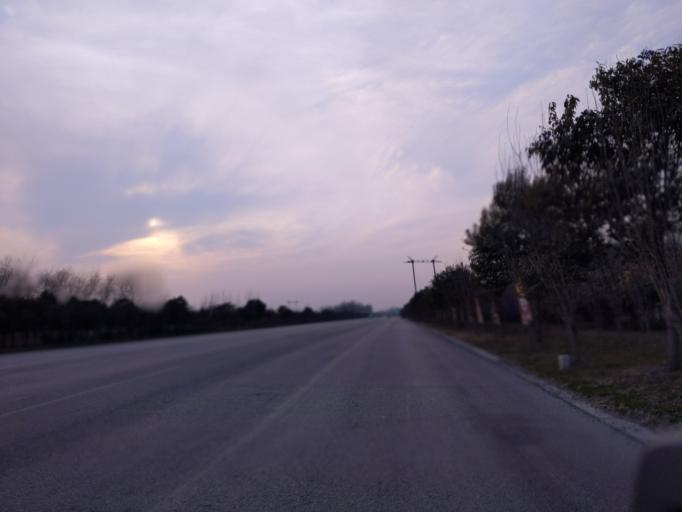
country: CN
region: Henan Sheng
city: Puyang
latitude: 35.8197
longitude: 114.9878
